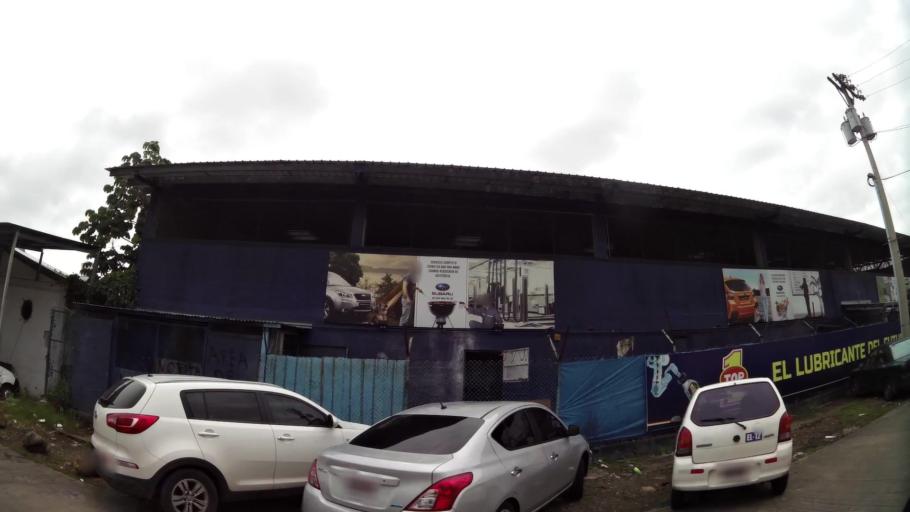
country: PA
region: Panama
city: Panama
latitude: 9.0012
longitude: -79.5275
